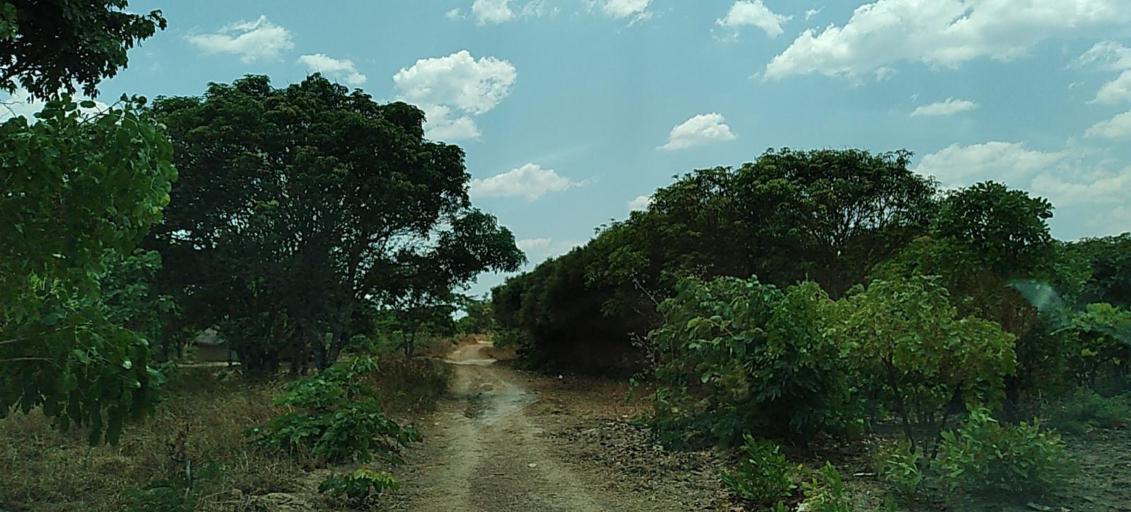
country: ZM
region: Copperbelt
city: Chililabombwe
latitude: -12.4560
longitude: 27.6721
